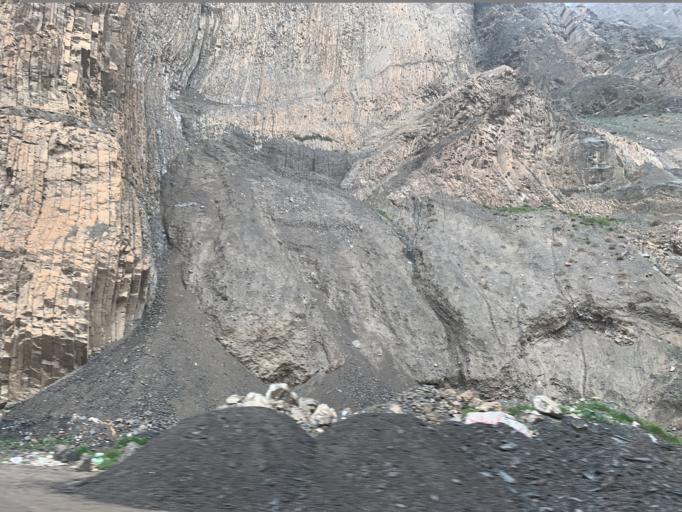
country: IR
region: Mazandaran
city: Amol
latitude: 36.1123
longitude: 52.2809
